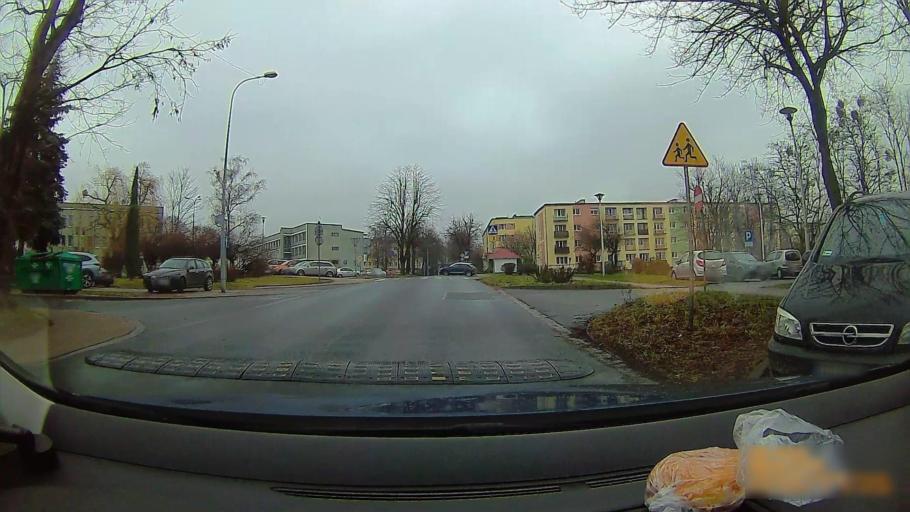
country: PL
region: Greater Poland Voivodeship
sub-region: Konin
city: Konin
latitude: 52.2262
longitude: 18.2511
